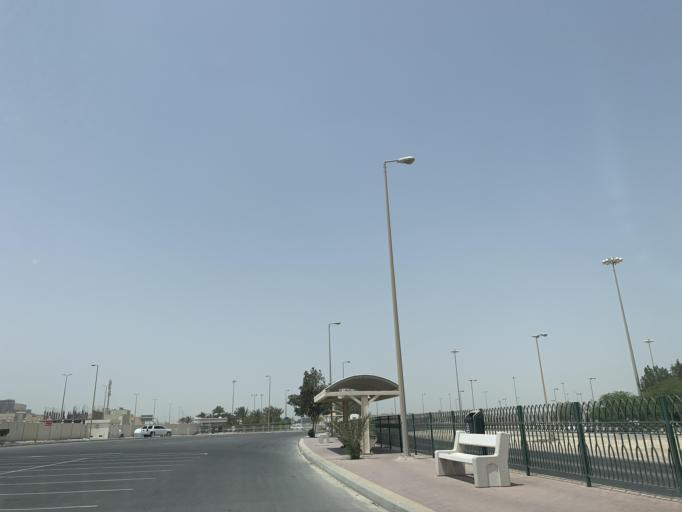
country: BH
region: Northern
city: Madinat `Isa
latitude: 26.1586
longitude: 50.5329
